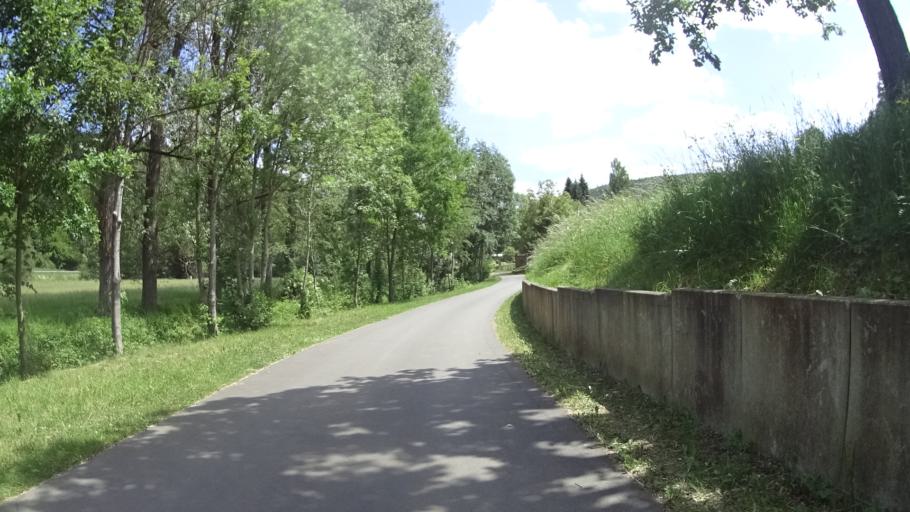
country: DE
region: Bavaria
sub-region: Regierungsbezirk Unterfranken
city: Neunkirchen
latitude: 49.6743
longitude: 9.3714
